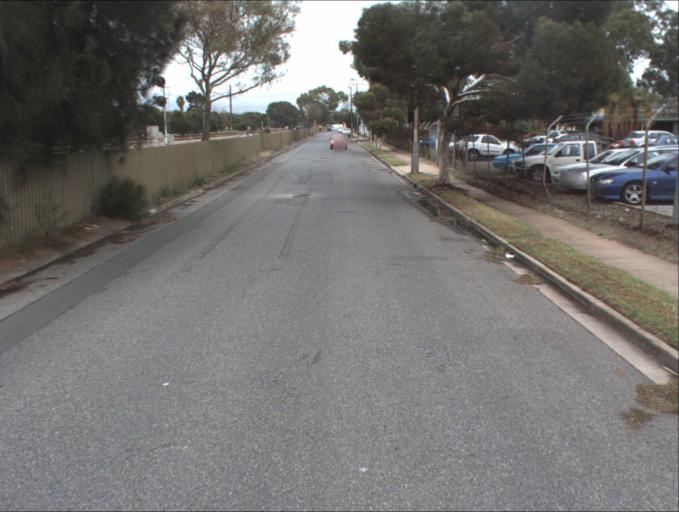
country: AU
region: South Australia
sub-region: Prospect
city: Prospect
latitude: -34.8788
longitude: 138.5826
